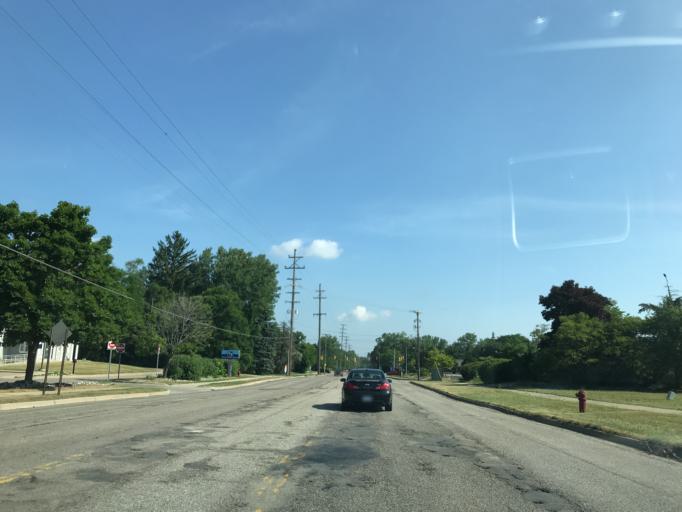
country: US
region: Michigan
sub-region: Ingham County
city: Okemos
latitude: 42.7202
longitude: -84.4275
